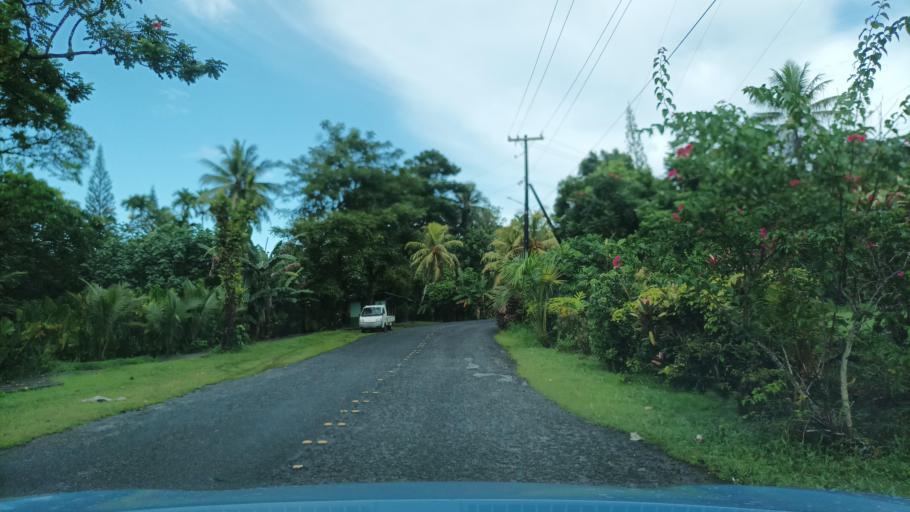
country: FM
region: Pohnpei
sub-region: Kolonia Municipality
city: Kolonia Town
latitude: 6.9496
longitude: 158.2019
